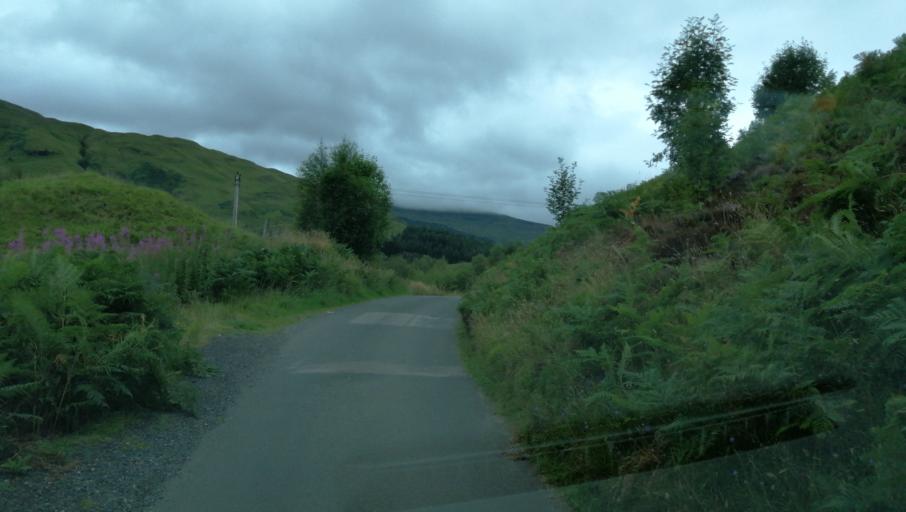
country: GB
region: Scotland
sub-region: Argyll and Bute
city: Garelochhead
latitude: 56.4234
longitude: -4.6740
